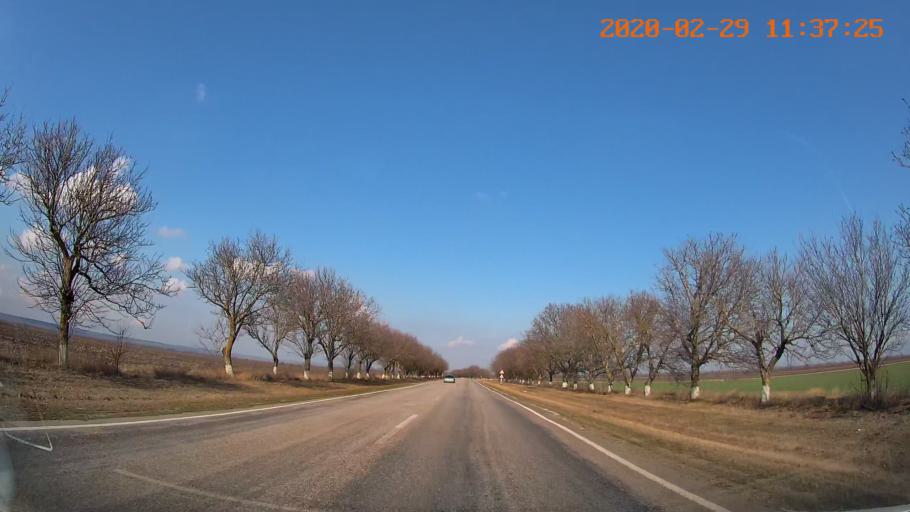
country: MD
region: Rezina
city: Saharna
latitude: 47.6114
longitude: 29.0463
